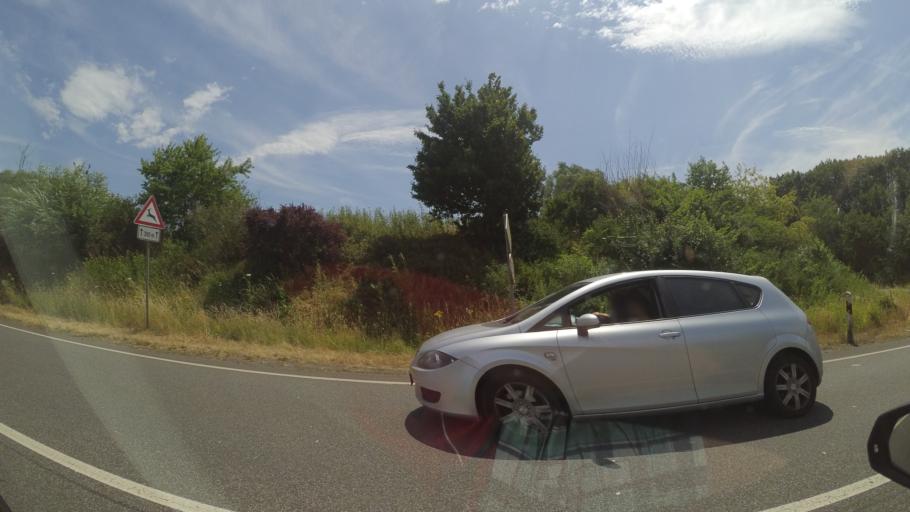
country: DE
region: Saarland
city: Saarwellingen
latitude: 49.3446
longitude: 6.7951
